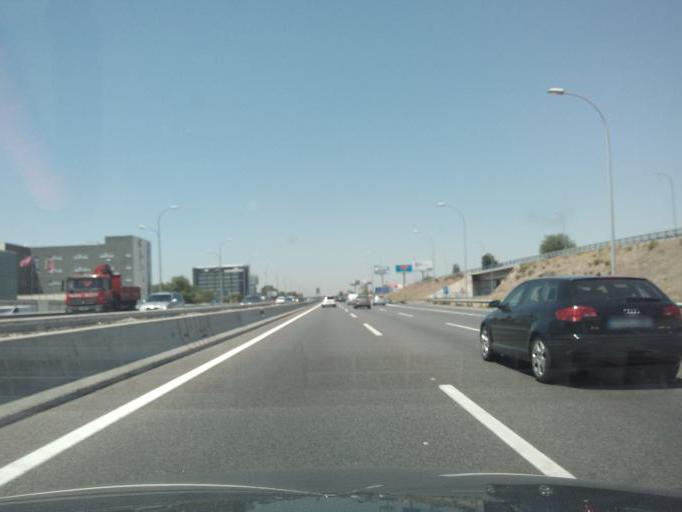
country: ES
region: Madrid
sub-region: Provincia de Madrid
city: San Fernando de Henares
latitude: 40.4477
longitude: -3.5409
